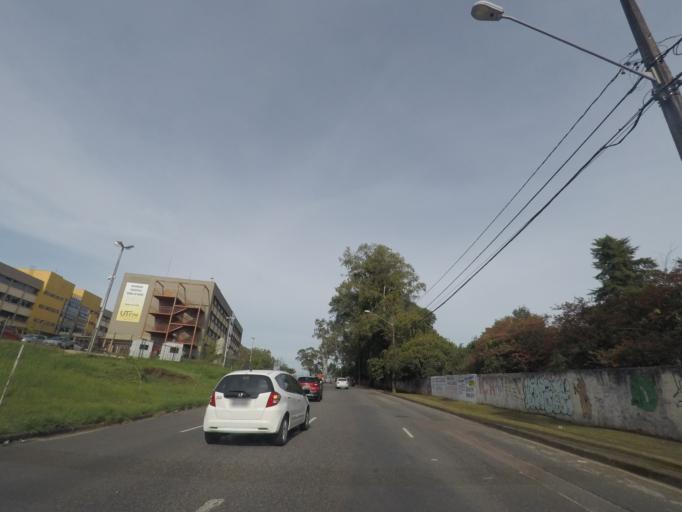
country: BR
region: Parana
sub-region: Curitiba
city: Curitiba
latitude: -25.4421
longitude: -49.3537
